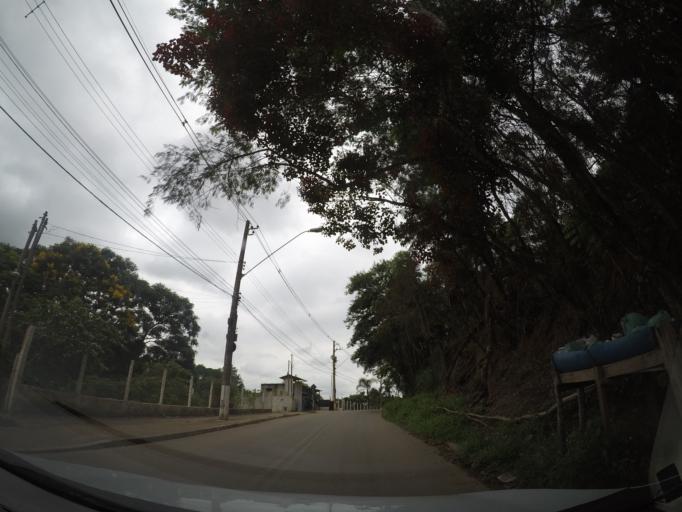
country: BR
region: Sao Paulo
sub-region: Aruja
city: Aruja
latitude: -23.3767
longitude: -46.3986
